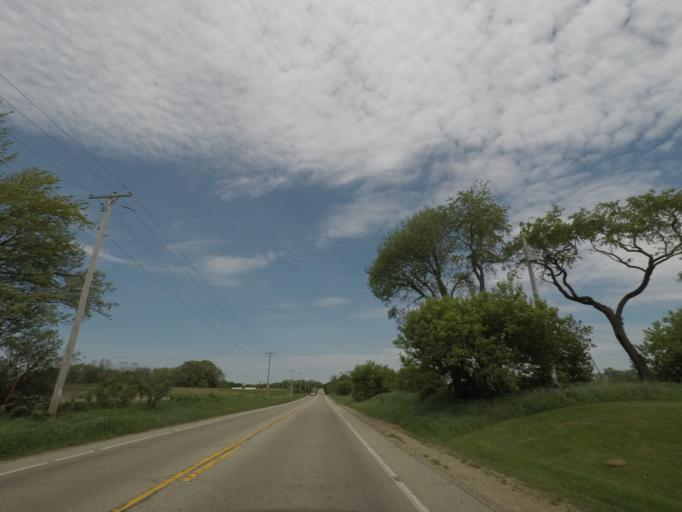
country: US
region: Wisconsin
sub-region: Green County
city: Brooklyn
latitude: 42.8671
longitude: -89.3496
